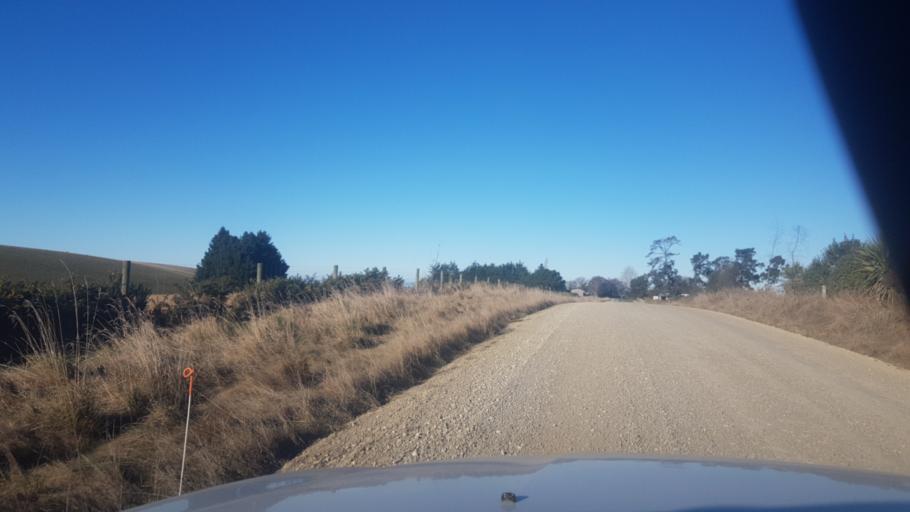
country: NZ
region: Canterbury
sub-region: Timaru District
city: Pleasant Point
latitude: -44.3706
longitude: 171.0742
